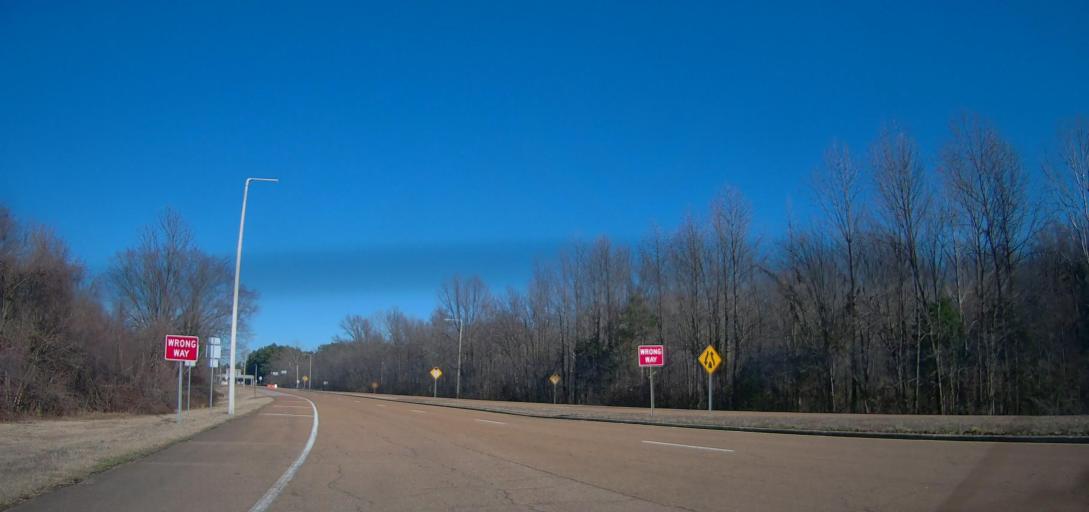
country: US
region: Tennessee
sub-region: Shelby County
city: Millington
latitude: 35.3210
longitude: -89.8720
